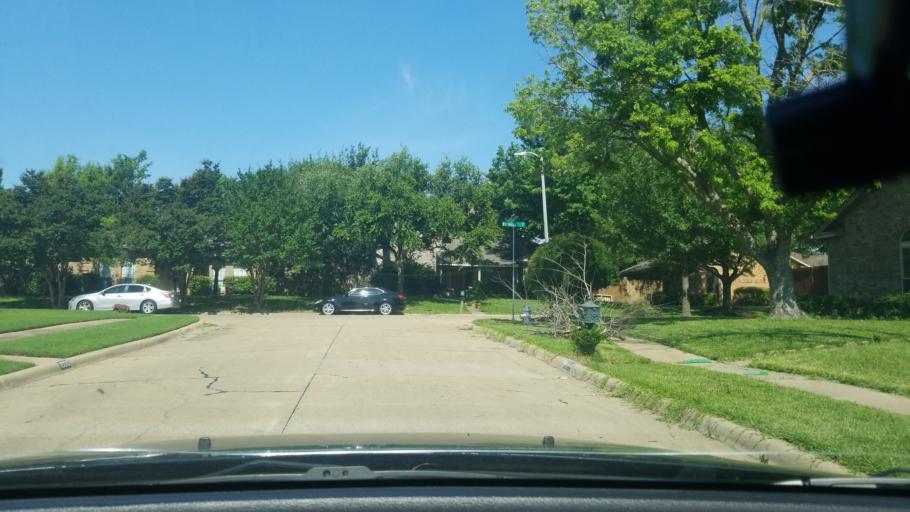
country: US
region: Texas
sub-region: Dallas County
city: Mesquite
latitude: 32.7731
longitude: -96.5849
